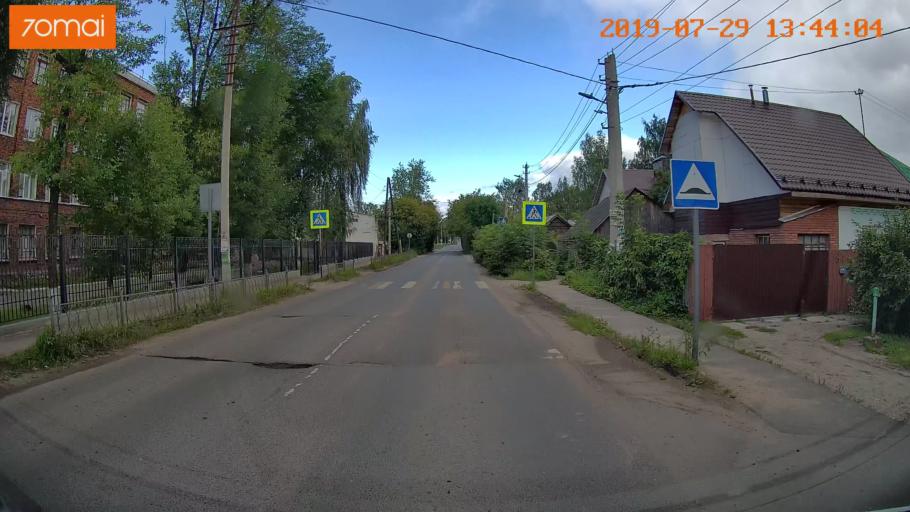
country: RU
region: Ivanovo
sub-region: Gorod Ivanovo
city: Ivanovo
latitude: 57.0083
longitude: 40.9310
